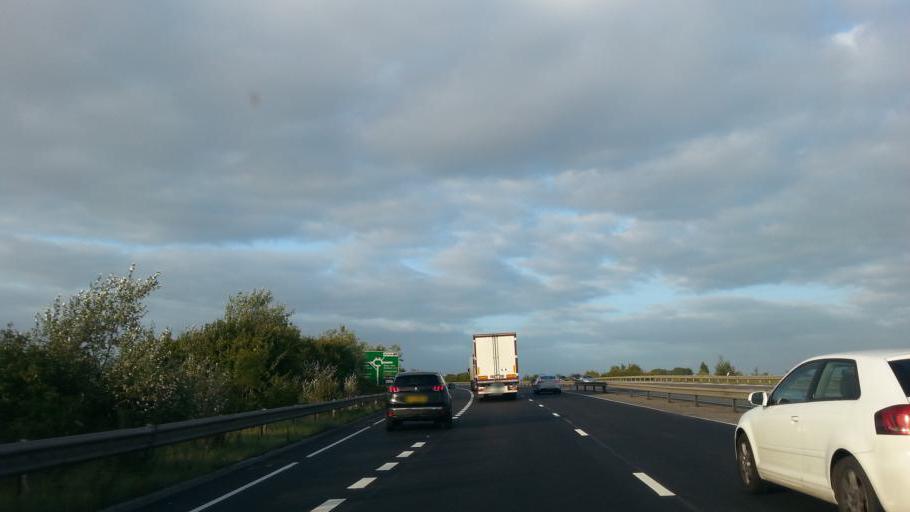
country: GB
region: England
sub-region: Oxfordshire
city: Yarnton
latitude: 51.7911
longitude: -1.2895
